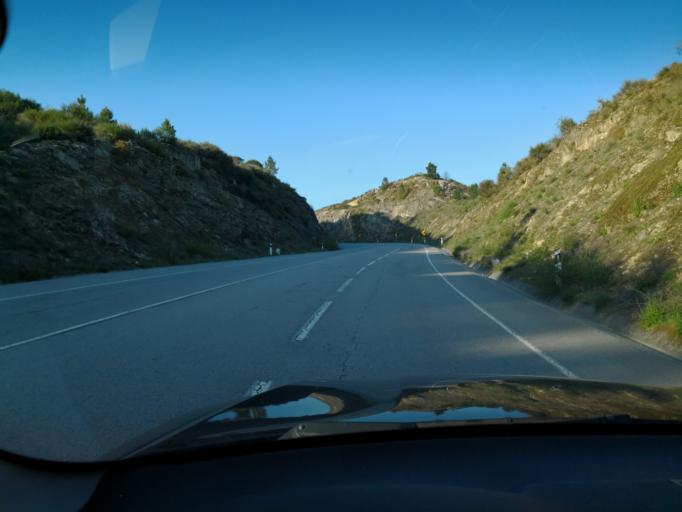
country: PT
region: Vila Real
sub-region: Vila Real
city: Vila Real
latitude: 41.3697
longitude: -7.7125
